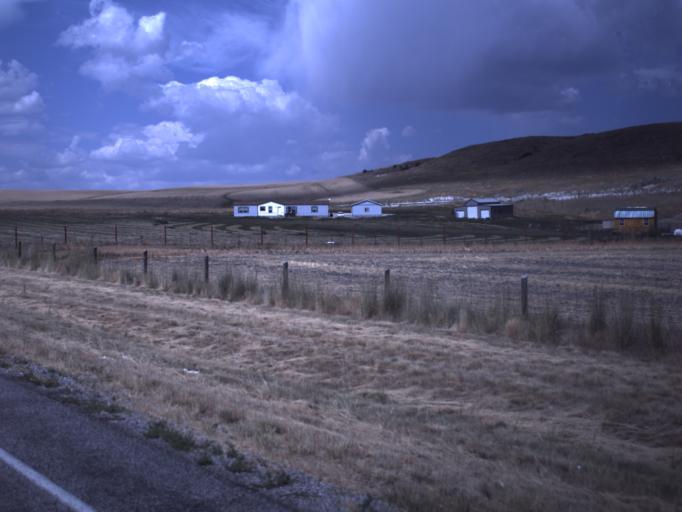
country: US
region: Utah
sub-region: Cache County
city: Mendon
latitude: 41.7738
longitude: -112.0181
